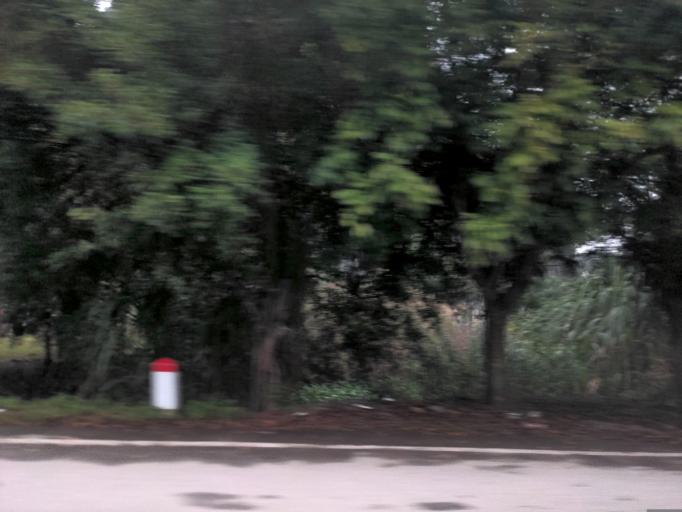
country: VN
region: Ninh Binh
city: Thanh Pho Ninh Binh
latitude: 20.2194
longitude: 105.9293
